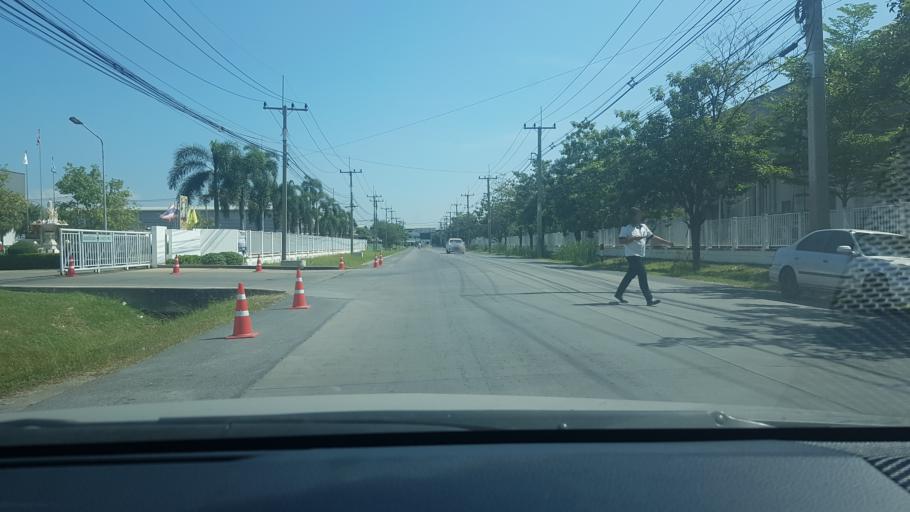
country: TH
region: Phra Nakhon Si Ayutthaya
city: Bang Pa-in
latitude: 14.2474
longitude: 100.5968
